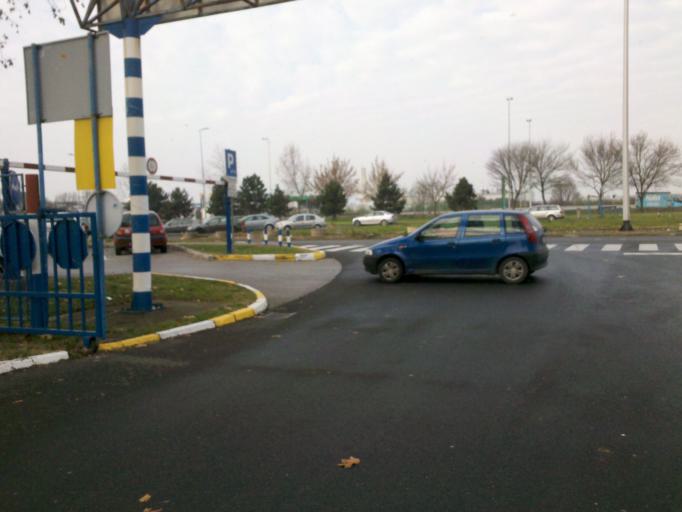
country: HR
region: Grad Zagreb
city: Dubrava
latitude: 45.8001
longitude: 16.0561
